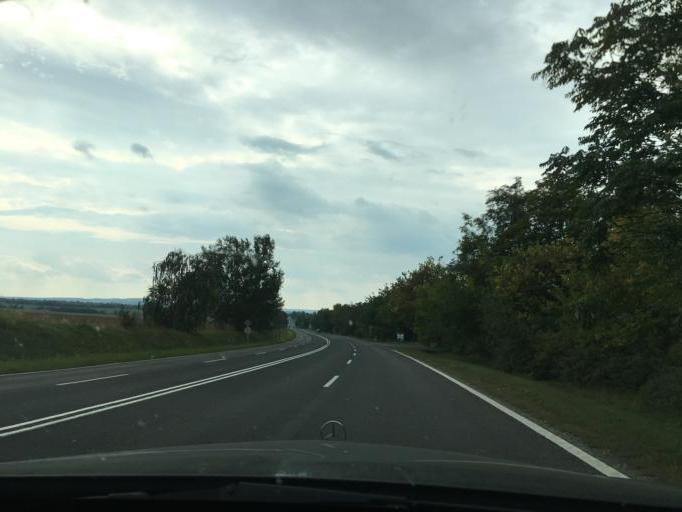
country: HU
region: Somogy
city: Balatonfoldvar
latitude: 46.8420
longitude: 17.8604
